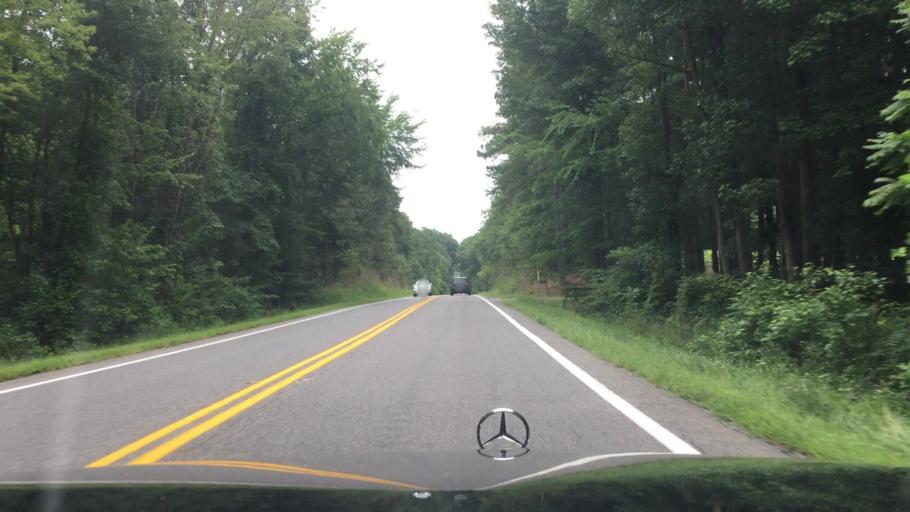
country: US
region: Virginia
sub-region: Prince Edward County
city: Farmville
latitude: 37.2731
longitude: -78.2783
